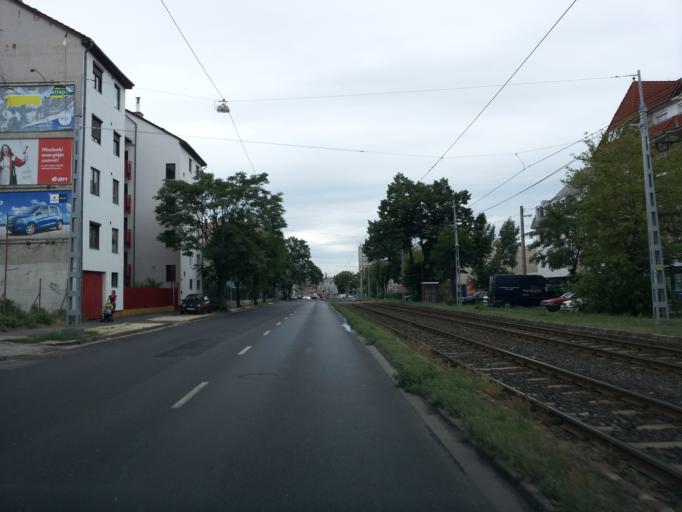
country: HU
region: Budapest
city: Budapest XIV. keruelet
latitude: 47.5160
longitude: 19.1181
